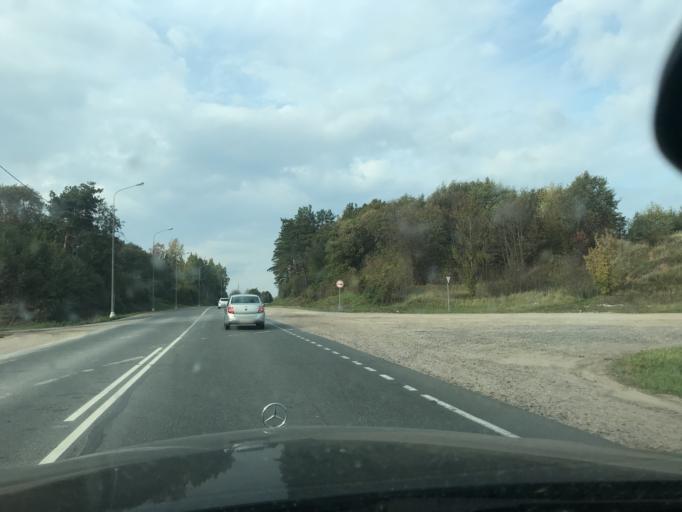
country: RU
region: Pskov
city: Ostrov
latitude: 57.3026
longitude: 28.3715
